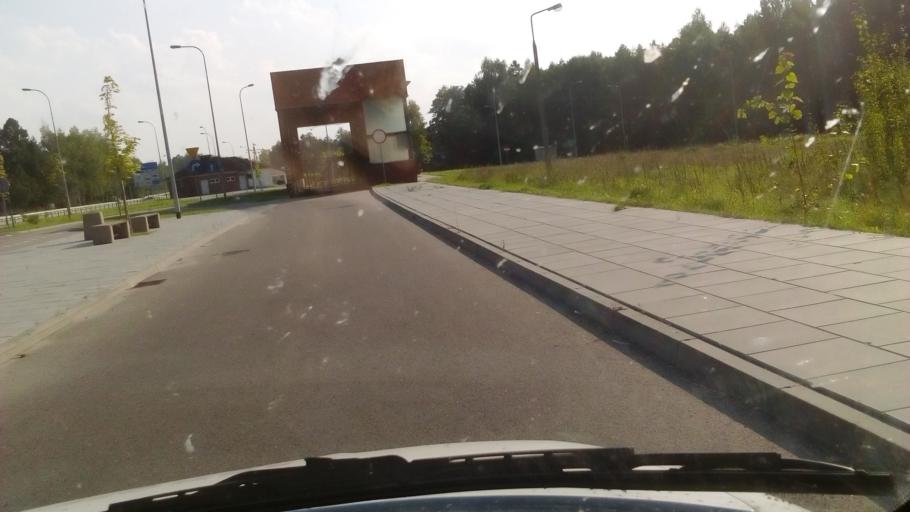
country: LT
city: Lazdijai
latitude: 54.1602
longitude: 23.4733
